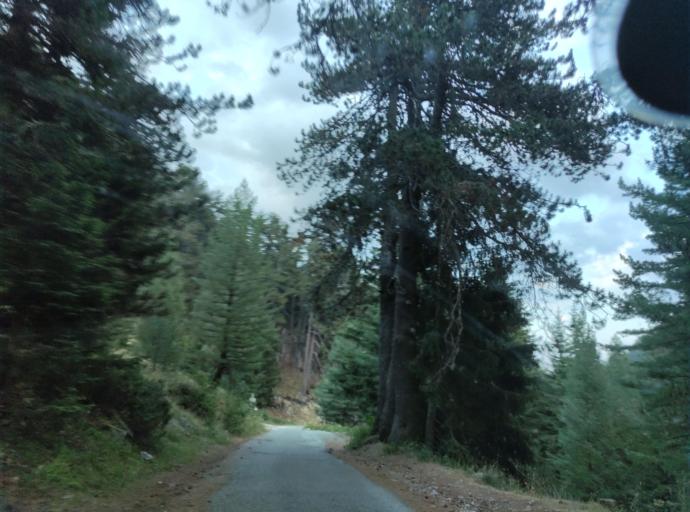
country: BG
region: Blagoevgrad
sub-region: Obshtina Bansko
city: Bansko
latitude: 41.7661
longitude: 23.4229
